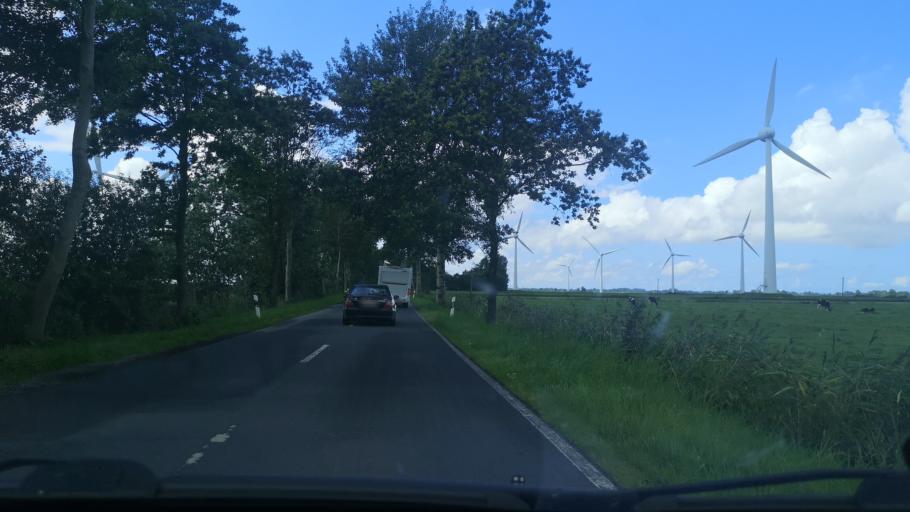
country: DE
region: Lower Saxony
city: Mulsum
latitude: 53.6427
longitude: 8.5792
